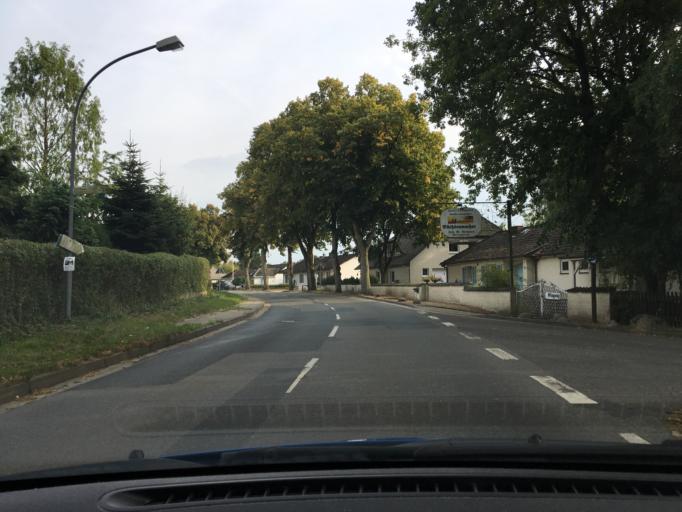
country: DE
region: Lower Saxony
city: Toppenstedt
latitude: 53.3007
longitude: 10.0919
